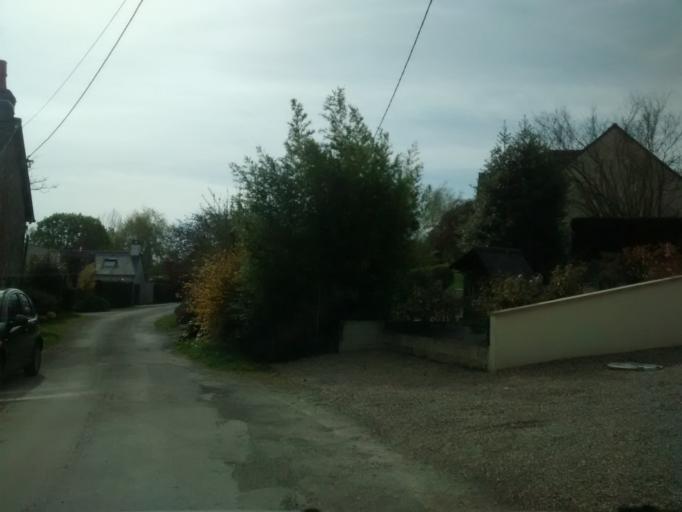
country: FR
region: Brittany
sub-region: Departement d'Ille-et-Vilaine
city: Noyal-sur-Vilaine
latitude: 48.1259
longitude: -1.5220
